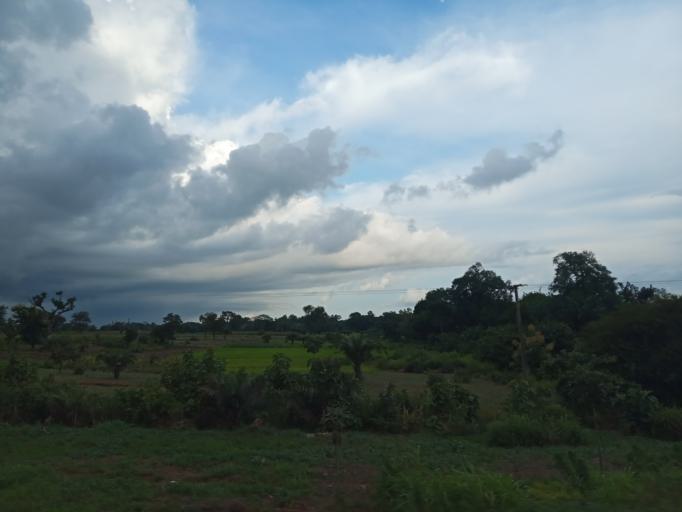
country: TG
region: Centrale
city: Sotouboua
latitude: 8.5810
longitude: 0.9854
